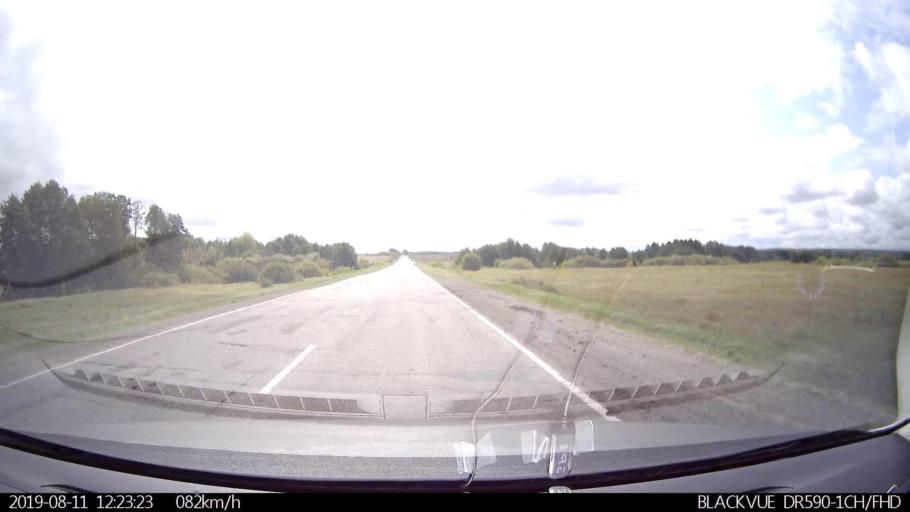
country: RU
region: Ulyanovsk
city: Ignatovka
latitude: 53.8964
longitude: 47.9505
